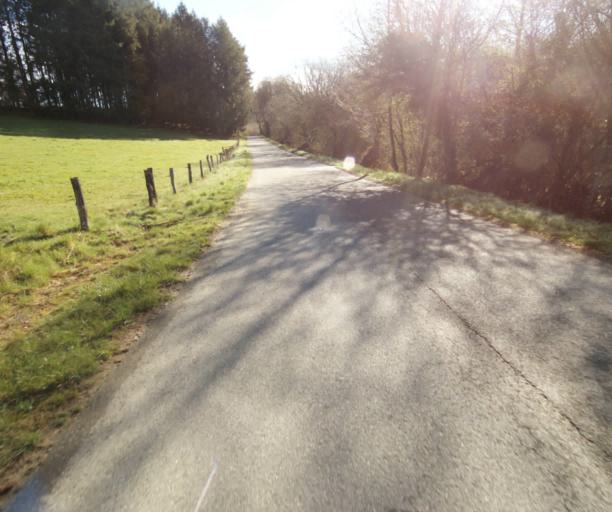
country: FR
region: Limousin
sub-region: Departement de la Correze
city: Laguenne
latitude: 45.2673
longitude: 1.8666
